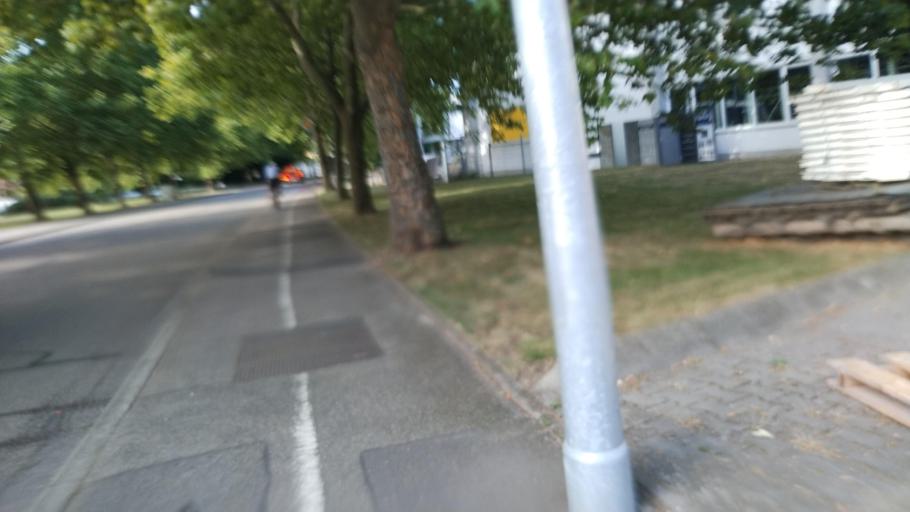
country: DE
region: Baden-Wuerttemberg
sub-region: Karlsruhe Region
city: Ettlingen
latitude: 48.9381
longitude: 8.3807
